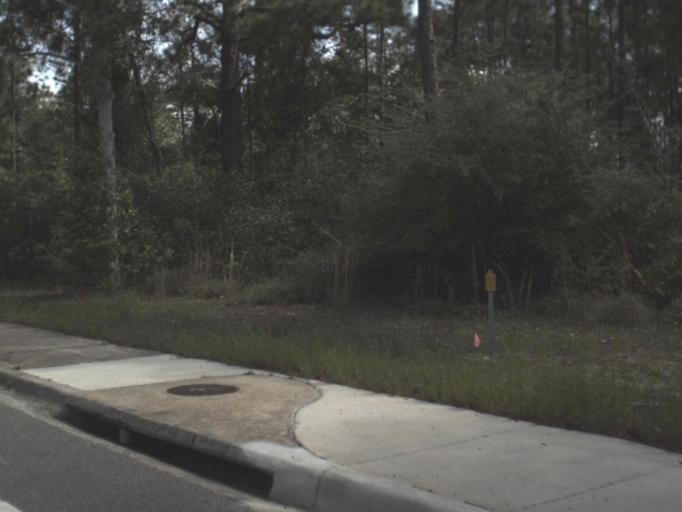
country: US
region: Florida
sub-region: Santa Rosa County
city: Navarre
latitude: 30.4257
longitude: -86.8671
